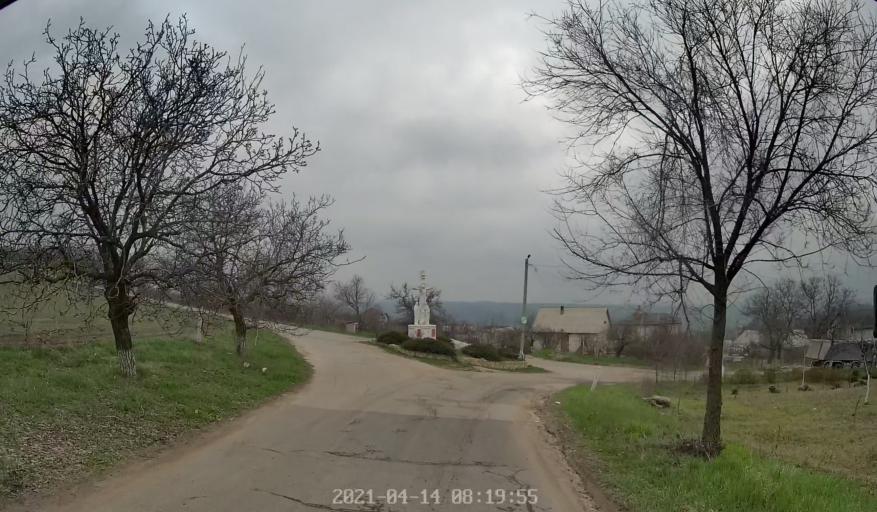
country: MD
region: Chisinau
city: Stauceni
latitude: 47.0640
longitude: 28.9194
